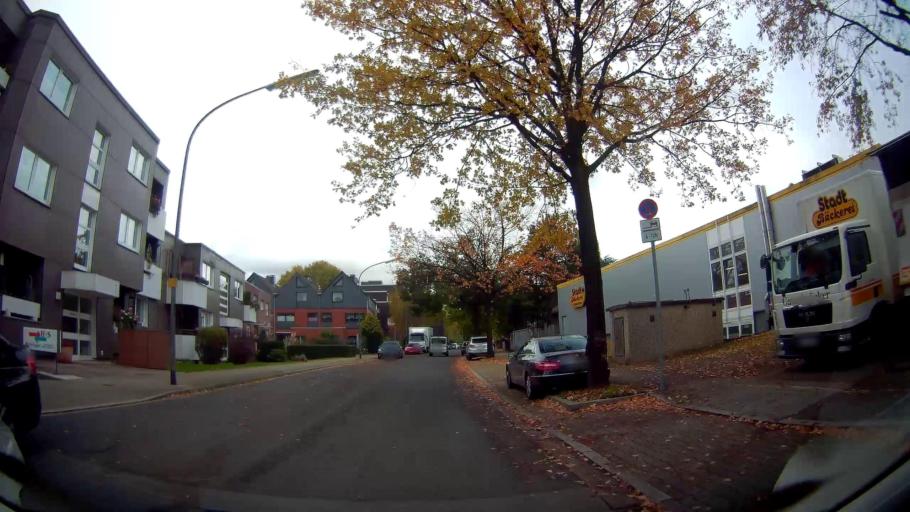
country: DE
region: North Rhine-Westphalia
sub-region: Regierungsbezirk Munster
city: Gelsenkirchen
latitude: 51.5529
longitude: 7.0857
